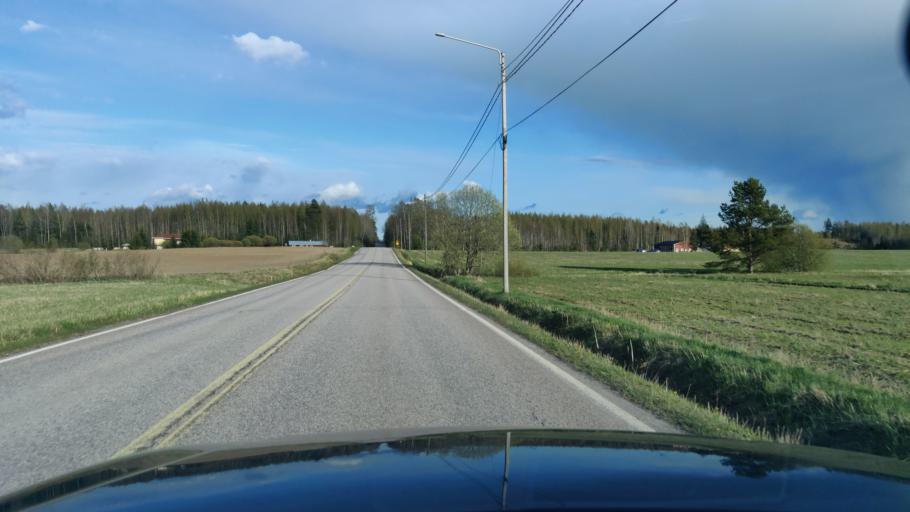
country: FI
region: Uusimaa
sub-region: Helsinki
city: Tuusula
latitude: 60.4672
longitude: 24.9922
